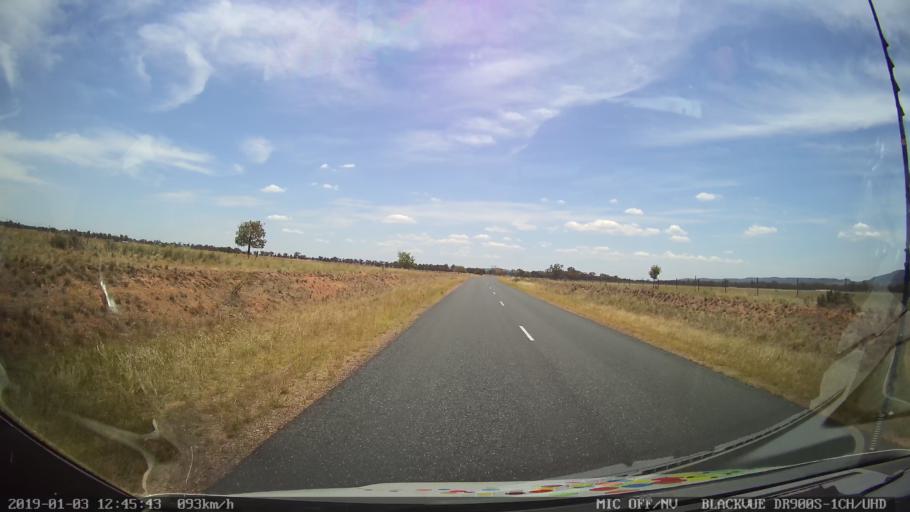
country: AU
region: New South Wales
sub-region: Weddin
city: Grenfell
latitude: -33.7459
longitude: 148.2257
